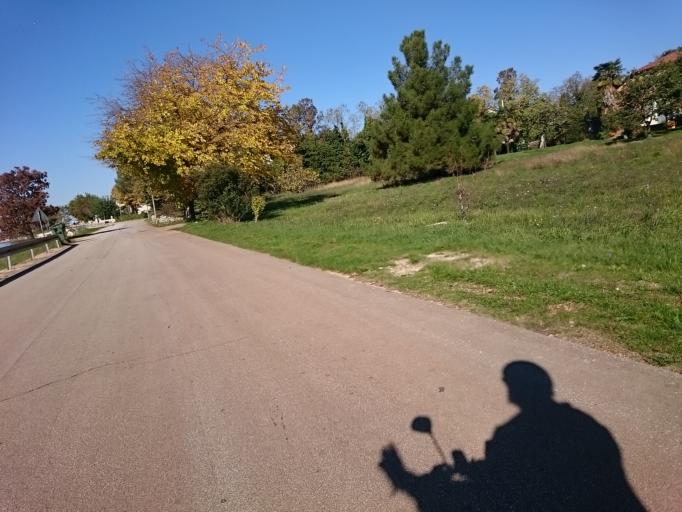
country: HR
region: Istarska
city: Umag
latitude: 45.3788
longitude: 13.5453
